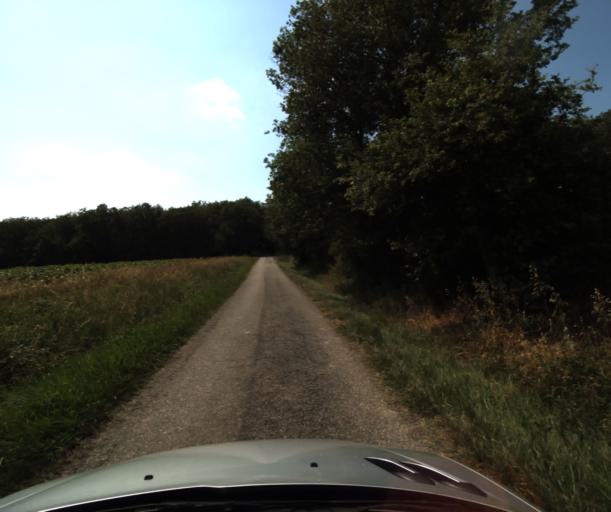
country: FR
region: Midi-Pyrenees
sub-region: Departement de la Haute-Garonne
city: Saint-Lys
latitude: 43.5303
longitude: 1.1560
